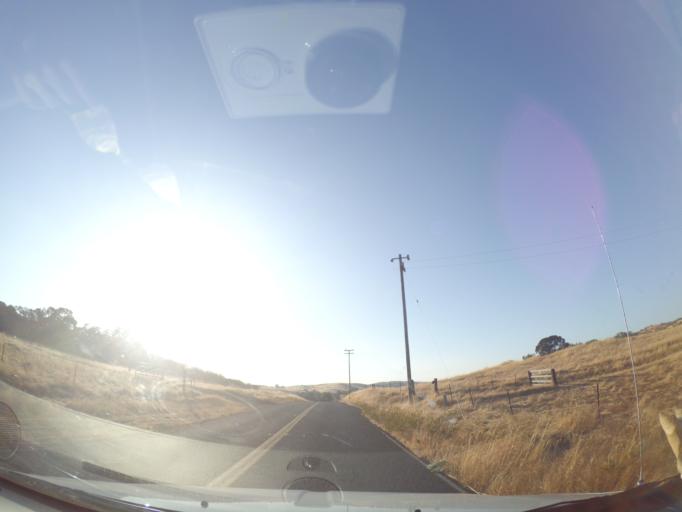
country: US
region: California
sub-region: Merced County
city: Planada
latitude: 37.4957
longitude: -120.2285
